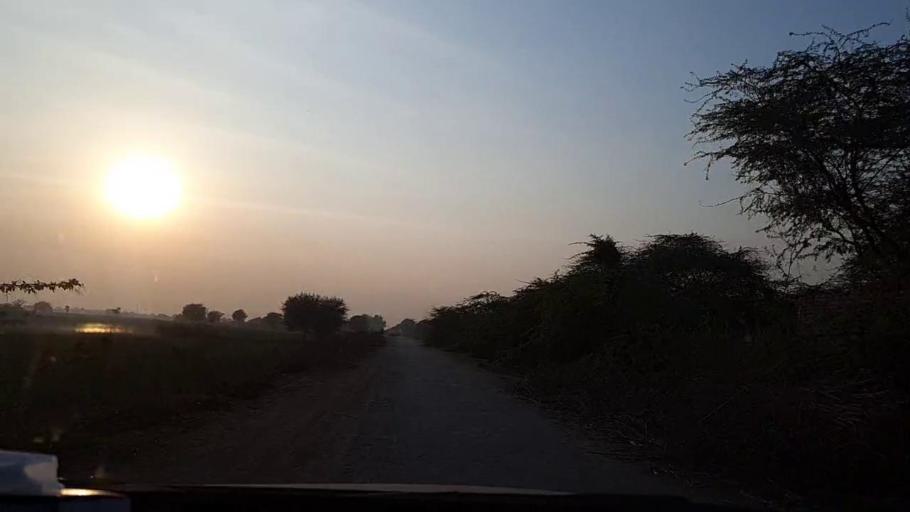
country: PK
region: Sindh
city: Tando Ghulam Ali
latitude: 25.1717
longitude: 68.9479
